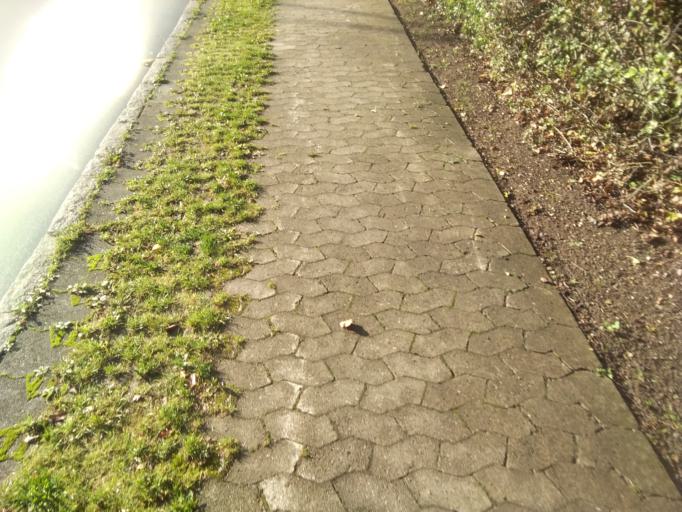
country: DK
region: Capital Region
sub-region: Gladsaxe Municipality
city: Buddinge
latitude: 55.7221
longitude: 12.5038
